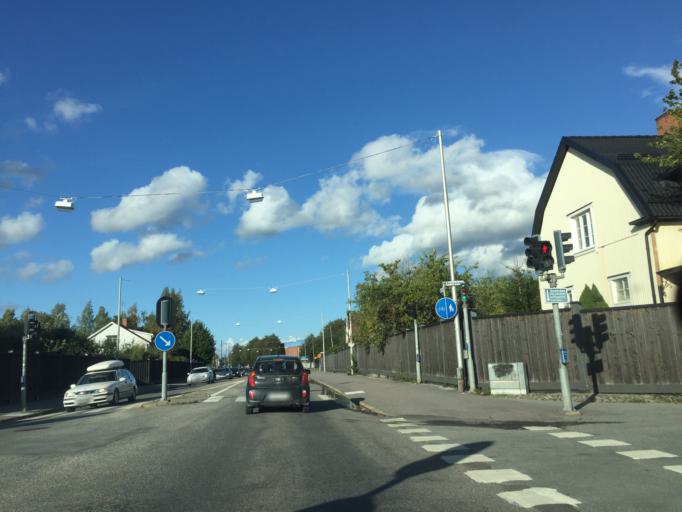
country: SE
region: OErebro
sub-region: Orebro Kommun
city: Orebro
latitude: 59.2862
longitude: 15.2039
